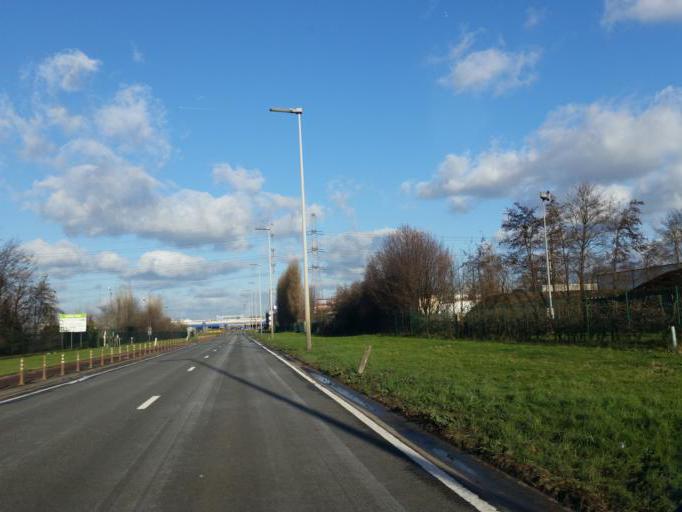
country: BE
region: Flanders
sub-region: Provincie Oost-Vlaanderen
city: Beveren
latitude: 51.2837
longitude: 4.2772
